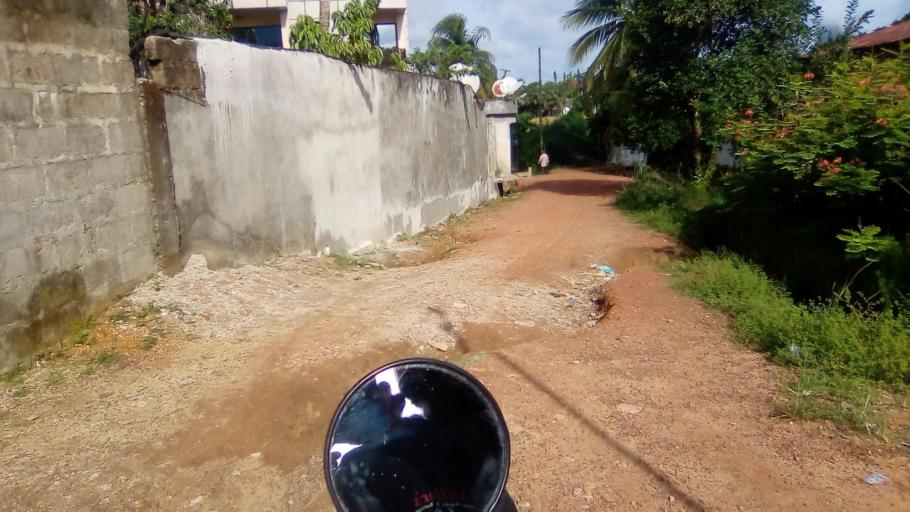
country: SL
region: Southern Province
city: Bo
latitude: 7.9554
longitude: -11.7622
